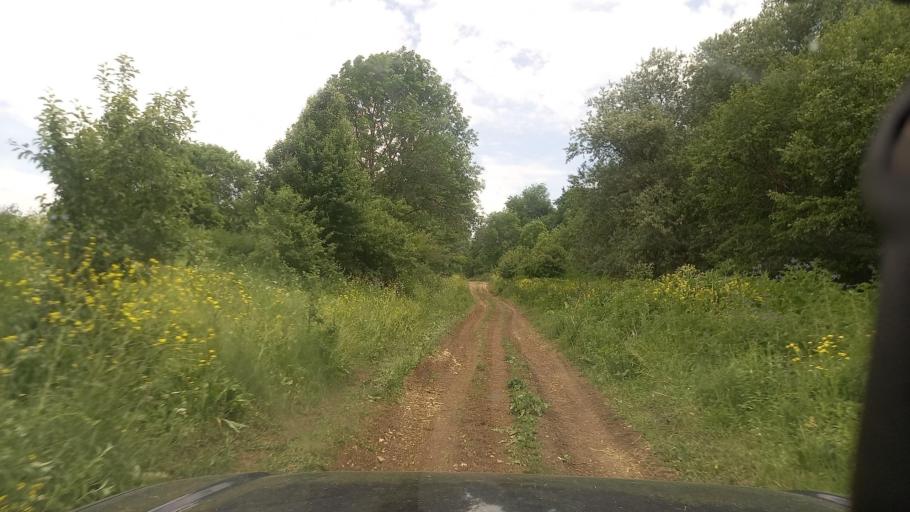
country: RU
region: Karachayevo-Cherkesiya
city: Pregradnaya
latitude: 44.0780
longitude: 41.2548
